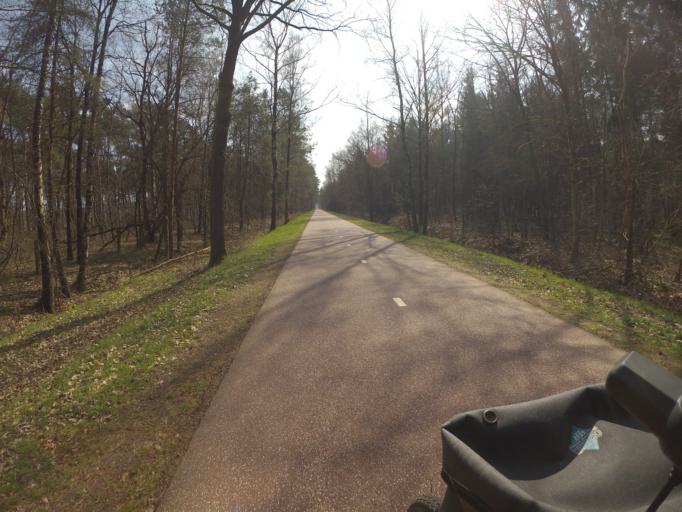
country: NL
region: North Brabant
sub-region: Gemeente Goirle
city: Goirle
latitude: 51.5496
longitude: 5.0241
